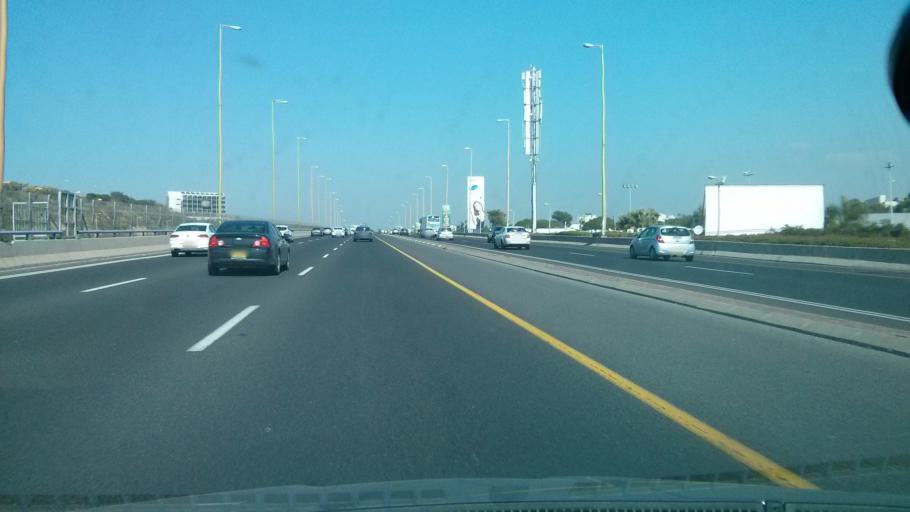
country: IL
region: Tel Aviv
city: Ramat Gan
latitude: 32.1045
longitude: 34.8055
